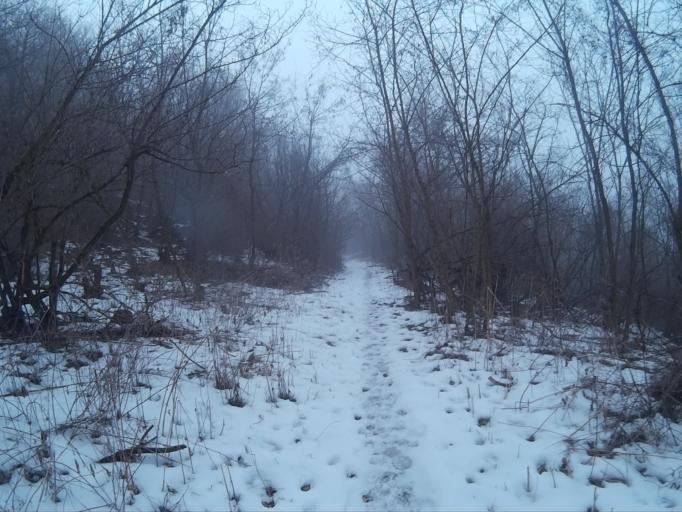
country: HU
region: Nograd
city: Matraverebely
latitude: 47.9820
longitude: 19.7629
